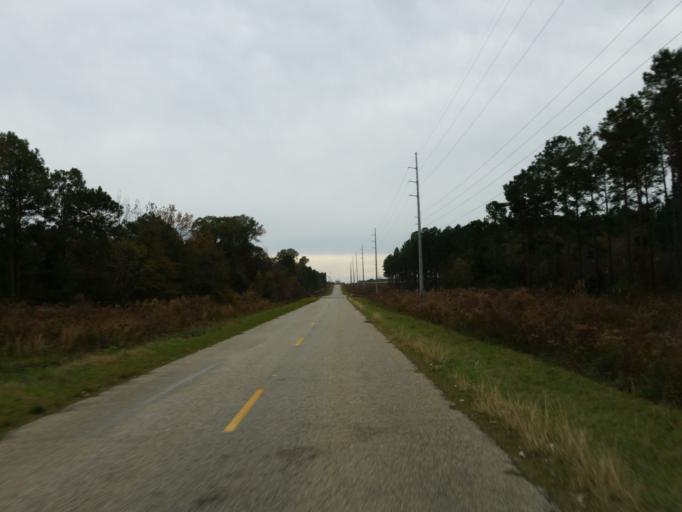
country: US
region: Georgia
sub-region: Dooly County
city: Vienna
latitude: 32.1353
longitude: -83.7612
